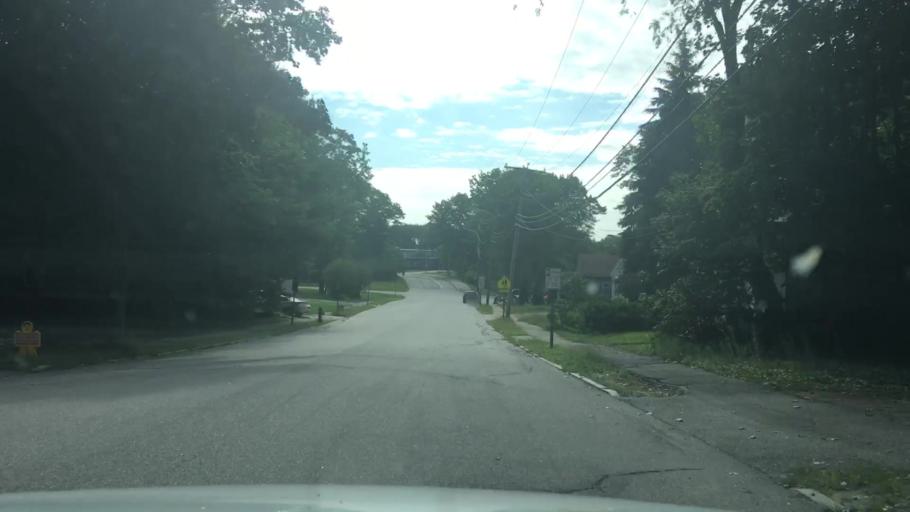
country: US
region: Maine
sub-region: Androscoggin County
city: Auburn
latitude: 44.0962
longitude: -70.2373
